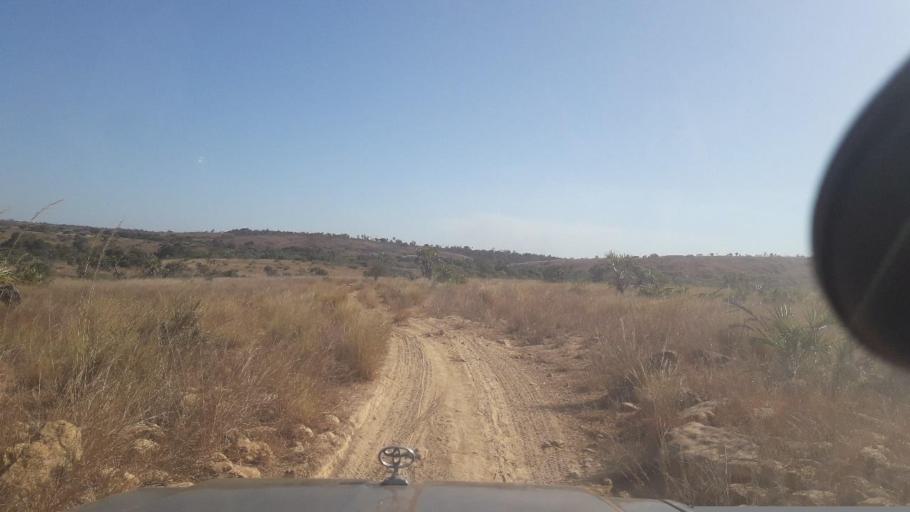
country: MG
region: Boeny
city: Sitampiky
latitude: -16.3743
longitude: 45.5935
